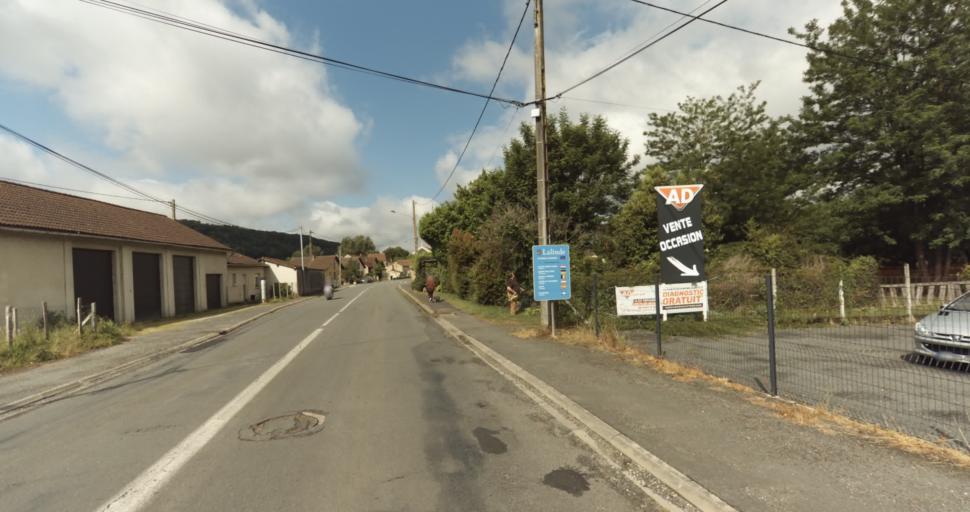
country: FR
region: Aquitaine
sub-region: Departement de la Dordogne
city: Lalinde
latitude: 44.8367
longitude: 0.7443
